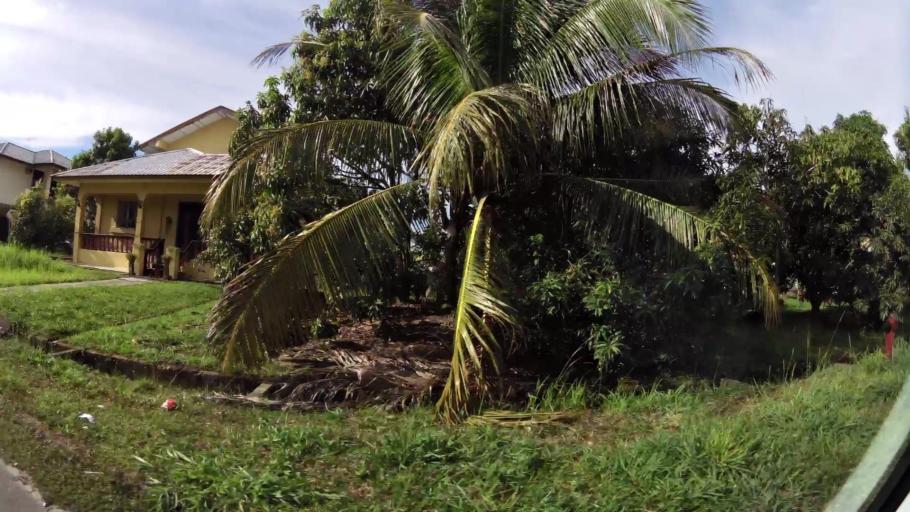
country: BN
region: Brunei and Muara
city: Bandar Seri Begawan
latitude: 4.9698
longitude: 115.0243
